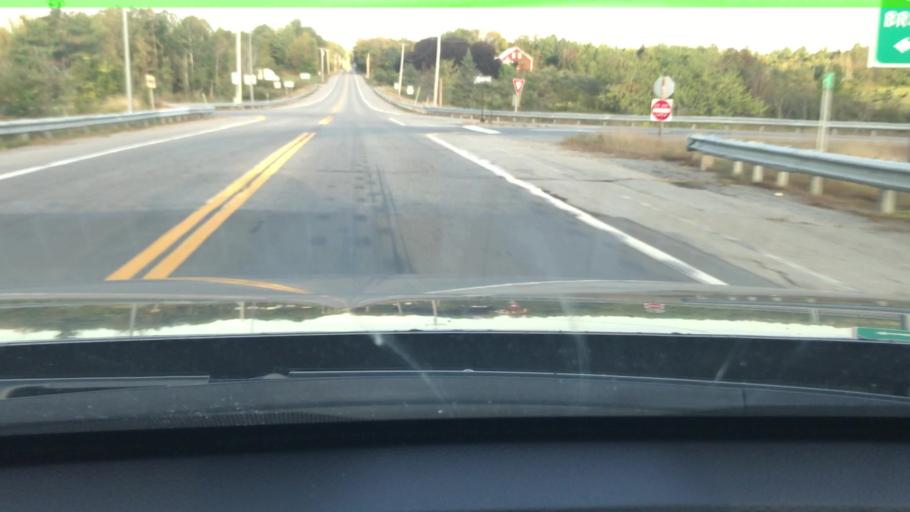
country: US
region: Maine
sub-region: Sagadahoc County
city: Richmond
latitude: 44.1000
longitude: -69.8704
